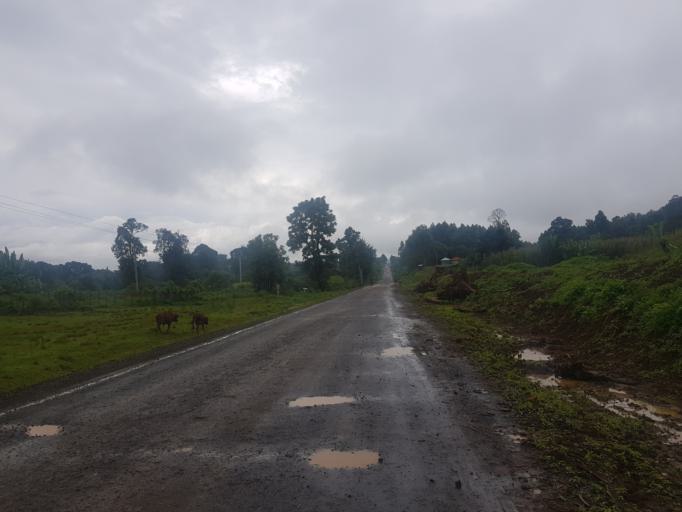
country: ET
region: Oromiya
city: Gore
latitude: 7.6886
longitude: 35.4972
